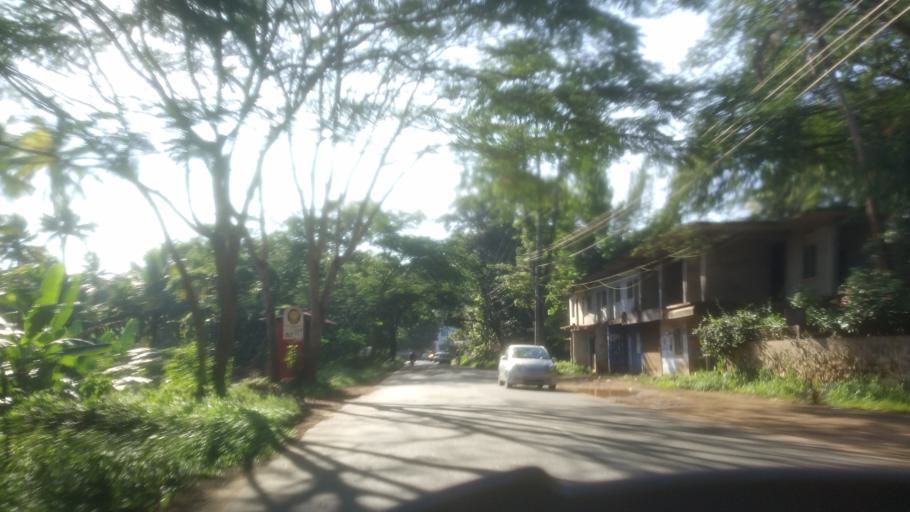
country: IN
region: Kerala
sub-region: Ernakulam
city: Muvattupuzha
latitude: 9.9799
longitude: 76.5392
